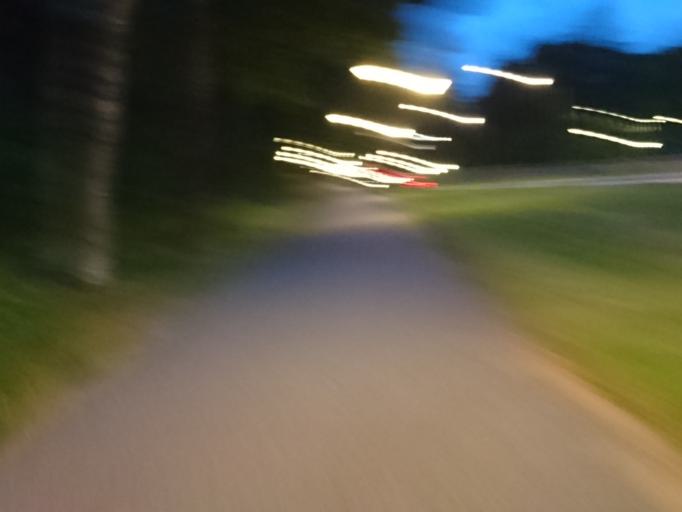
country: SE
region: Stockholm
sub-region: Huddinge Kommun
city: Huddinge
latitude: 59.2784
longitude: 17.9738
